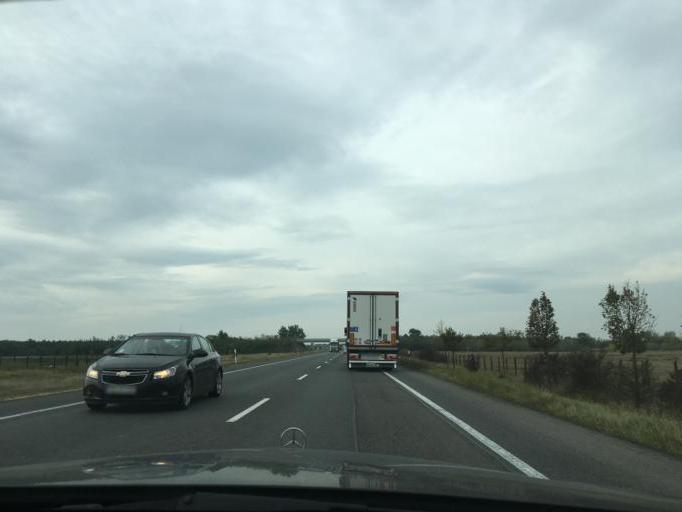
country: HU
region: Gyor-Moson-Sopron
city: Rajka
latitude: 47.9644
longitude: 17.1728
